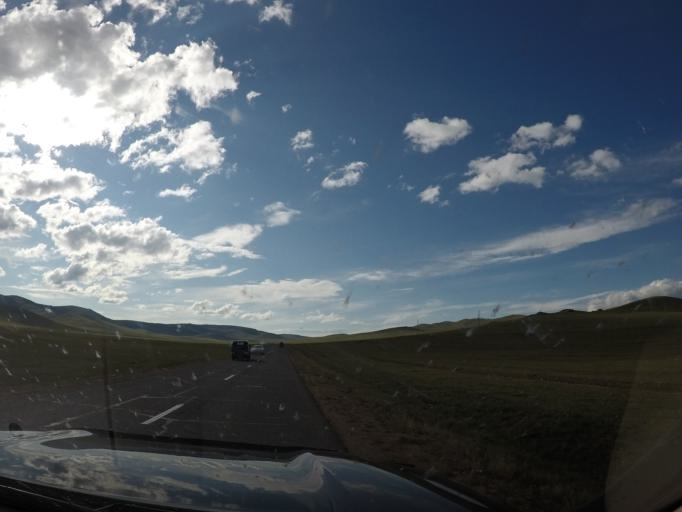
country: MN
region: Hentiy
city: Modot
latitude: 47.7643
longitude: 108.9026
